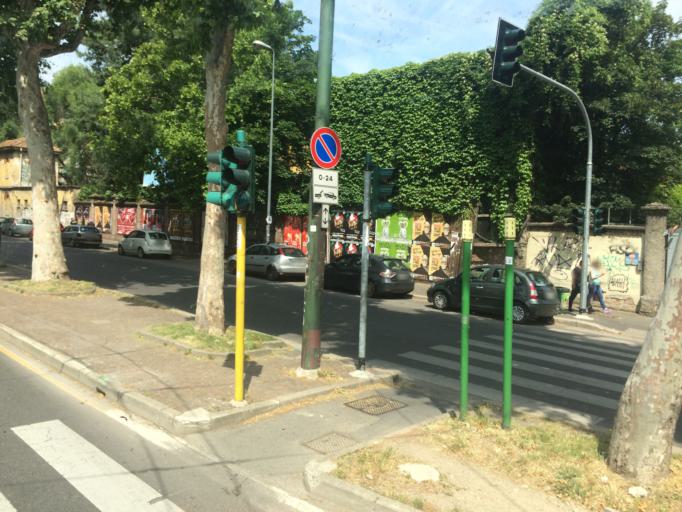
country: IT
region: Lombardy
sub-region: Citta metropolitana di Milano
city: Milano
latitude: 45.4969
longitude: 9.1773
